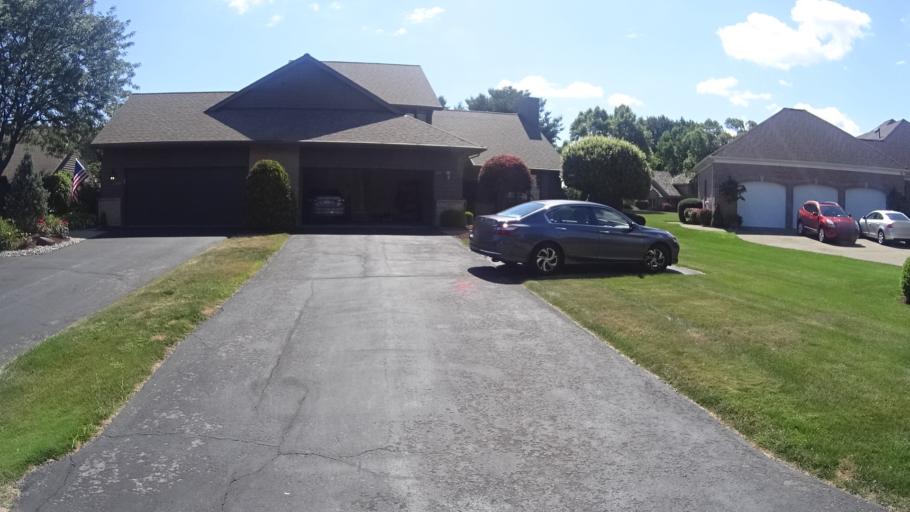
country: US
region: Ohio
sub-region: Erie County
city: Sandusky
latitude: 41.4074
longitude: -82.6490
